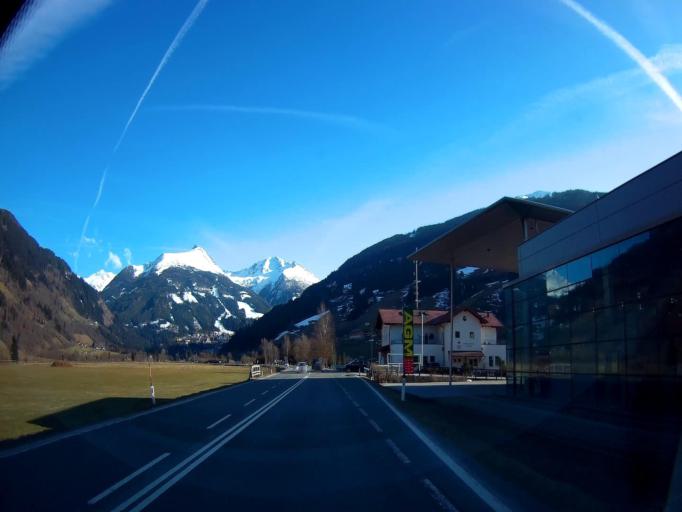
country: AT
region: Salzburg
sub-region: Politischer Bezirk Sankt Johann im Pongau
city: Bad Hofgastein
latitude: 47.1501
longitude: 13.1135
